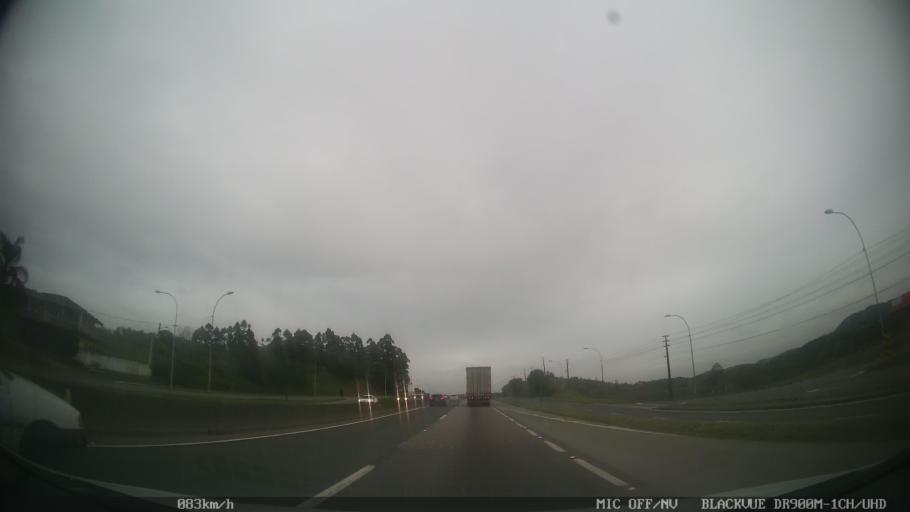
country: BR
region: Santa Catarina
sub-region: Penha
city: Penha
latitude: -26.7695
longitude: -48.6863
